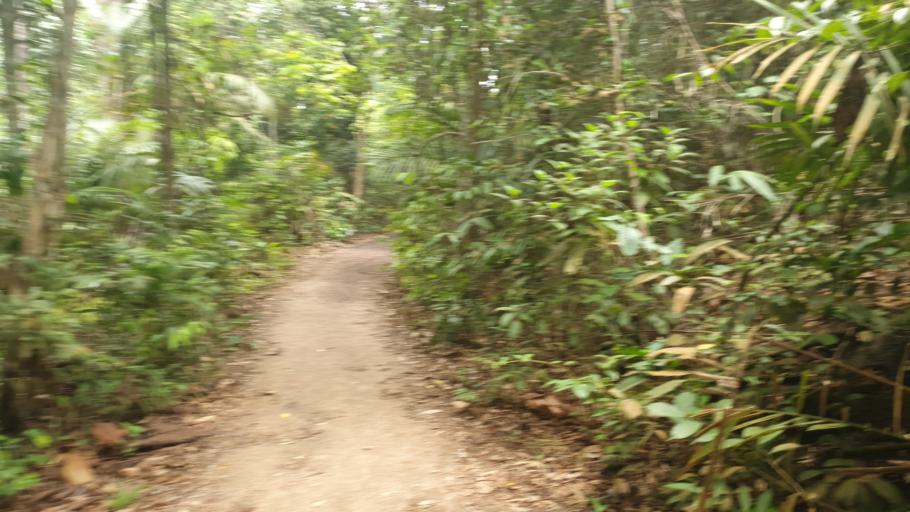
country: SG
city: Singapore
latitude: 1.3563
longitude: 103.8166
